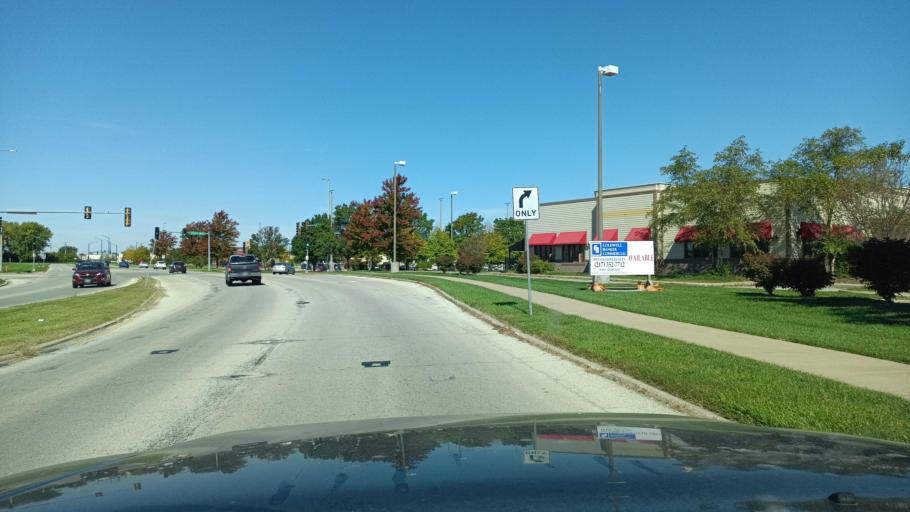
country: US
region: Illinois
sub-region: Champaign County
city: Champaign
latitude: 40.1394
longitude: -88.2440
